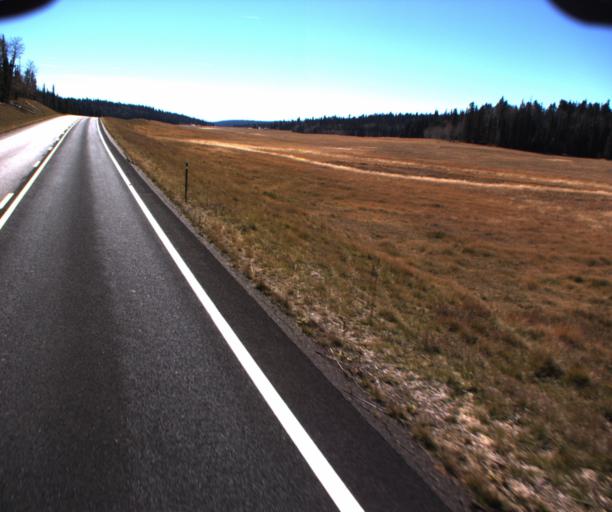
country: US
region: Arizona
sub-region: Coconino County
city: Grand Canyon
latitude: 36.4368
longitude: -112.1344
